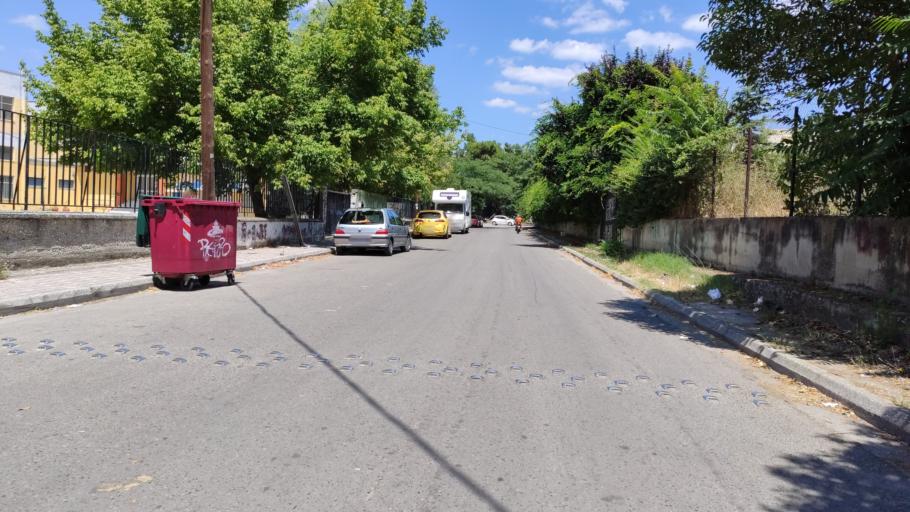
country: GR
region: East Macedonia and Thrace
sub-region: Nomos Rodopis
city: Komotini
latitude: 41.1216
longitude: 25.3974
